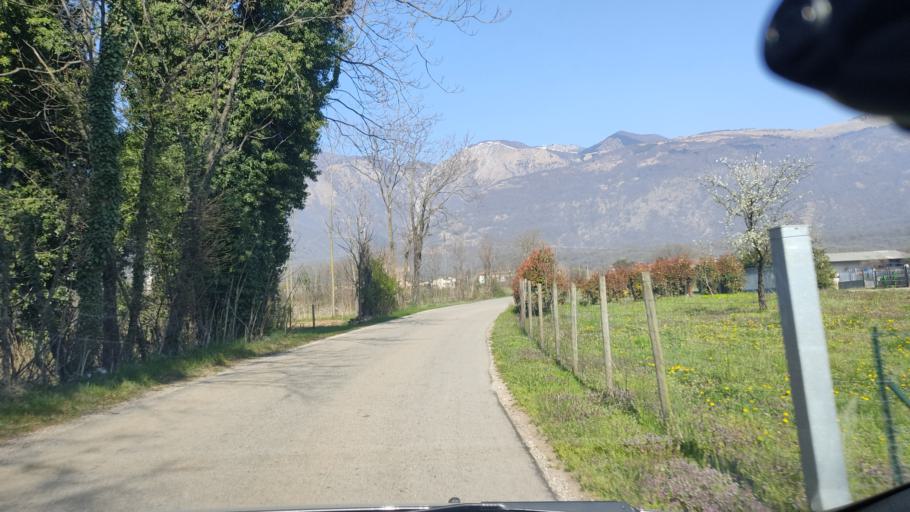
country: IT
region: Friuli Venezia Giulia
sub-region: Provincia di Pordenone
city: Budoia
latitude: 46.0504
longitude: 12.5457
